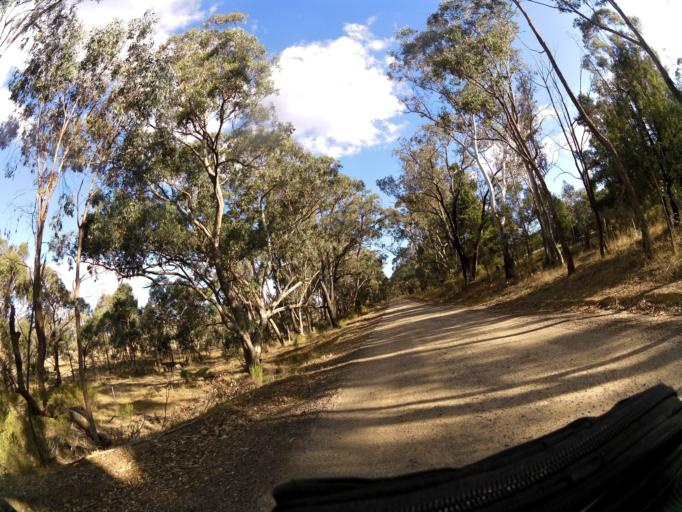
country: AU
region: Victoria
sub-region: Greater Bendigo
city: Kennington
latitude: -37.0121
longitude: 144.8089
